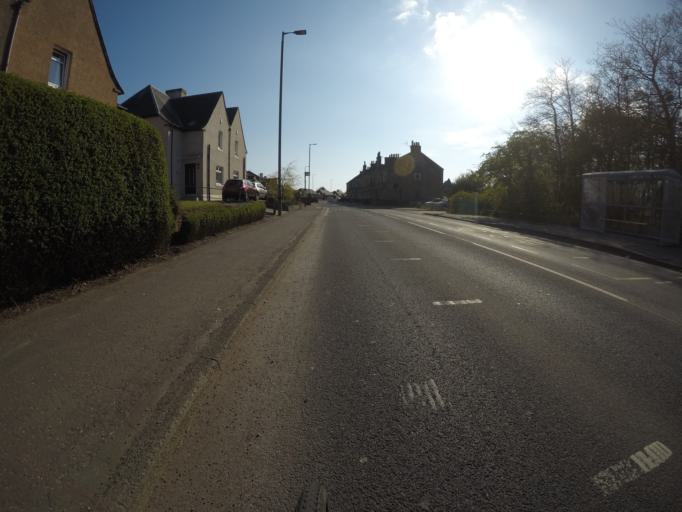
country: GB
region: Scotland
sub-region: North Ayrshire
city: Kilwinning
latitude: 55.6533
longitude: -4.7146
